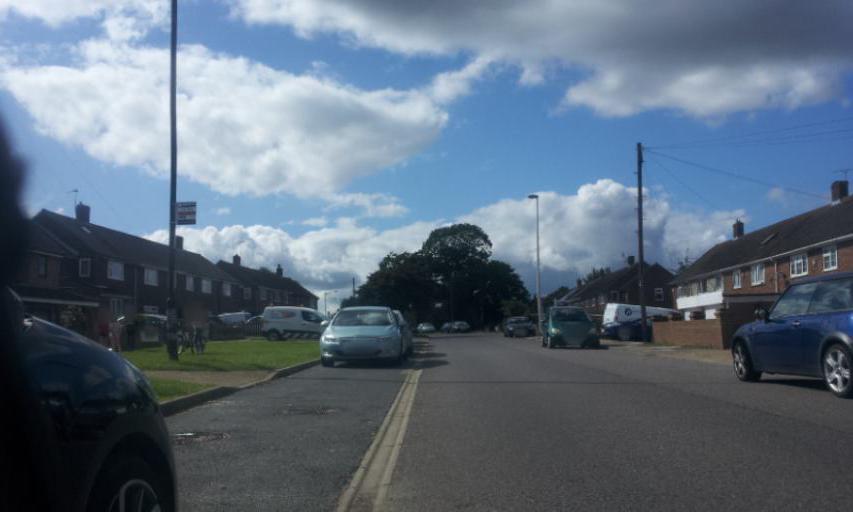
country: GB
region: England
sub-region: Kent
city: Chatham
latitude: 51.3478
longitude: 0.5164
